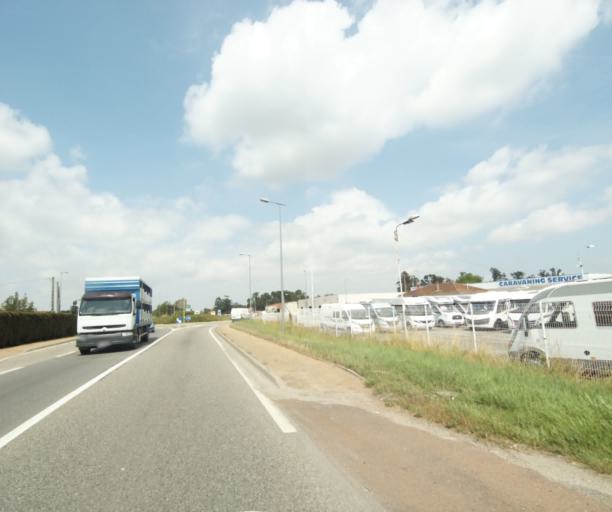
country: FR
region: Midi-Pyrenees
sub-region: Departement du Tarn-et-Garonne
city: Albias
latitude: 44.0593
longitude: 1.4079
